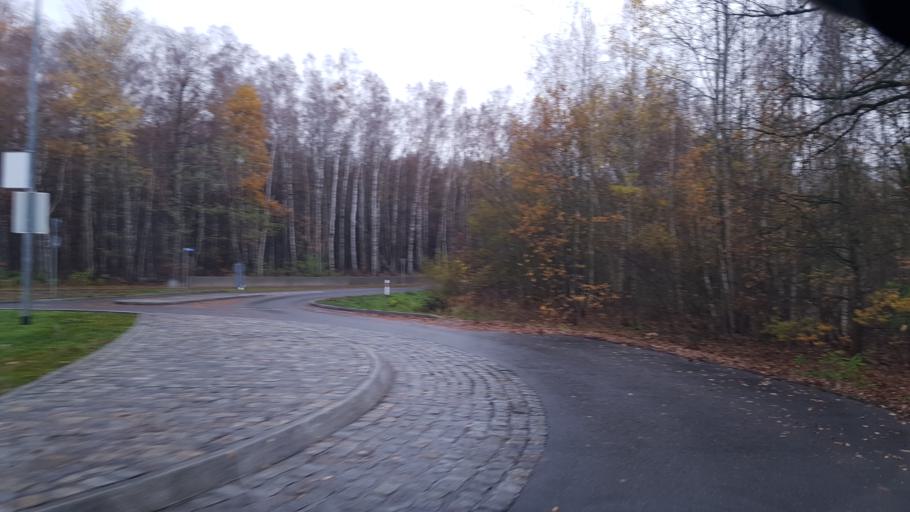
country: DE
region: Brandenburg
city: Lauchhammer
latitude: 51.4835
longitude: 13.7644
